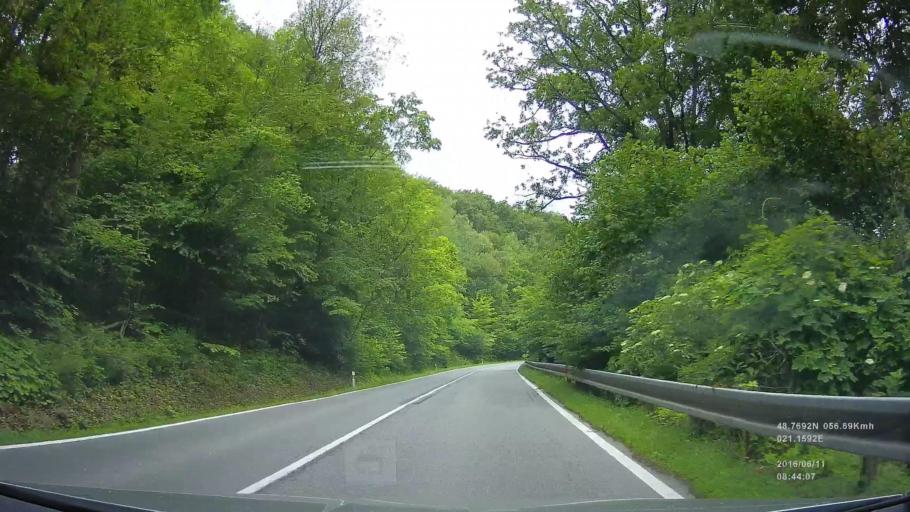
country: SK
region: Kosicky
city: Kosice
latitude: 48.7572
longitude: 21.1897
